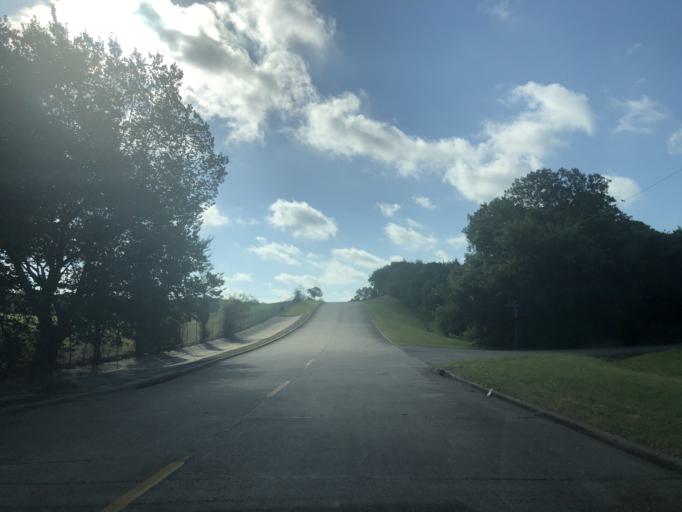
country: US
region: Texas
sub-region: Dallas County
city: Duncanville
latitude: 32.6681
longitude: -96.9239
